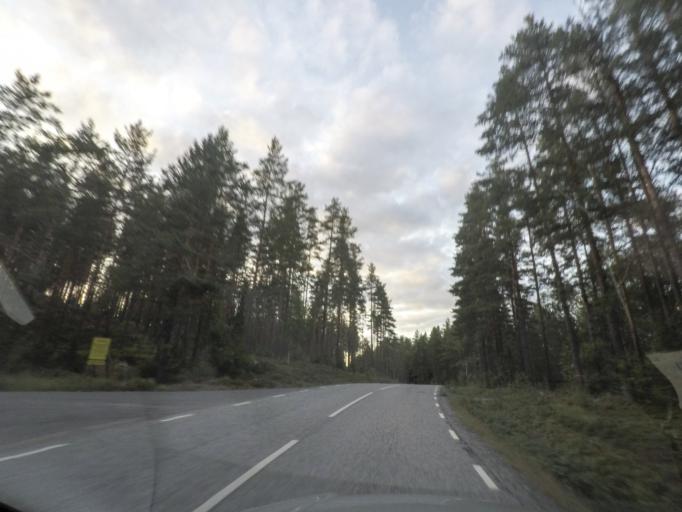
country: SE
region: OErebro
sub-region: Hallefors Kommun
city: Haellefors
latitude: 59.8704
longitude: 14.5354
